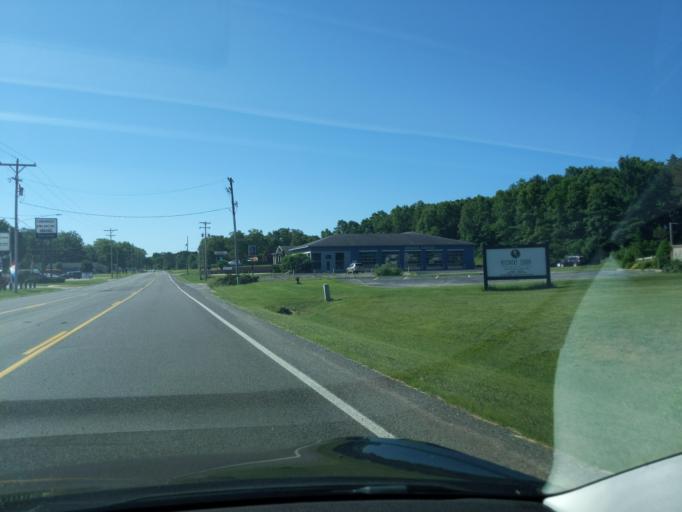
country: US
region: Michigan
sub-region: Muskegon County
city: Whitehall
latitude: 43.4066
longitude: -86.3146
